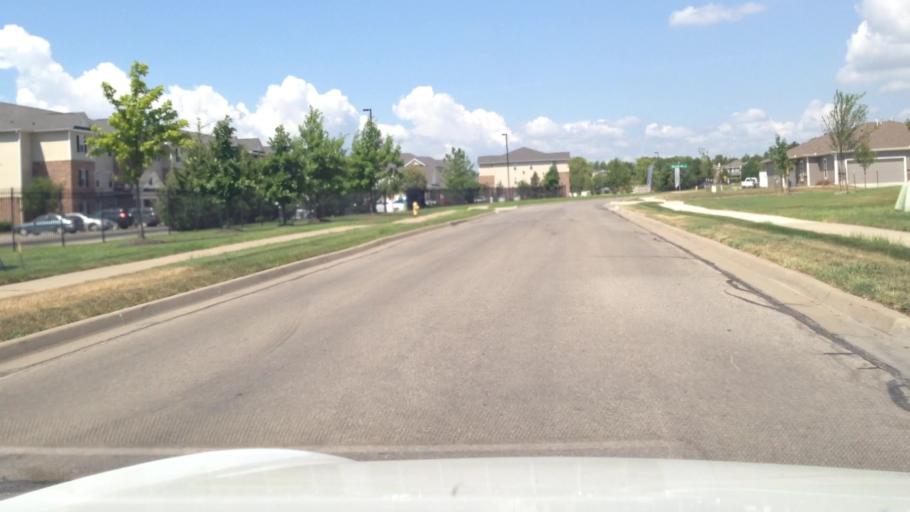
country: US
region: Kansas
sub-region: Douglas County
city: Lawrence
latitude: 38.9407
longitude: -95.2939
